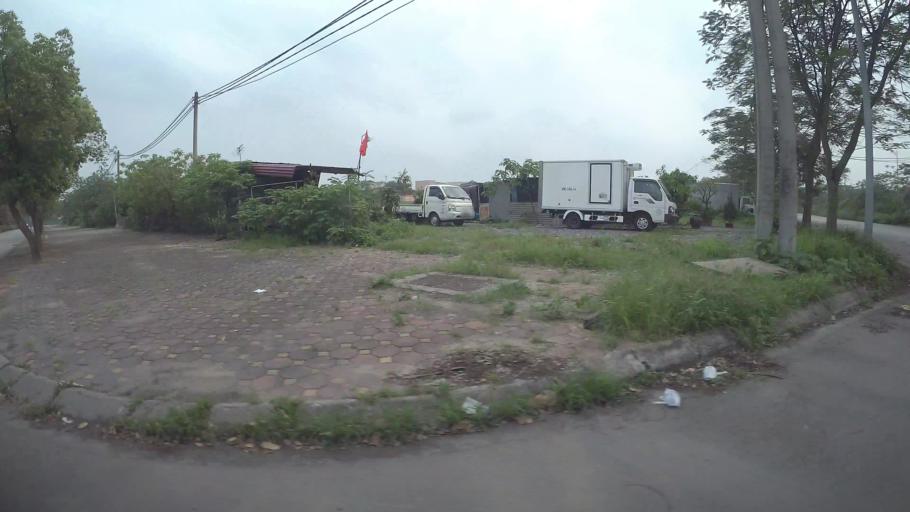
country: VN
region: Ha Noi
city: Trau Quy
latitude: 21.0672
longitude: 105.9014
